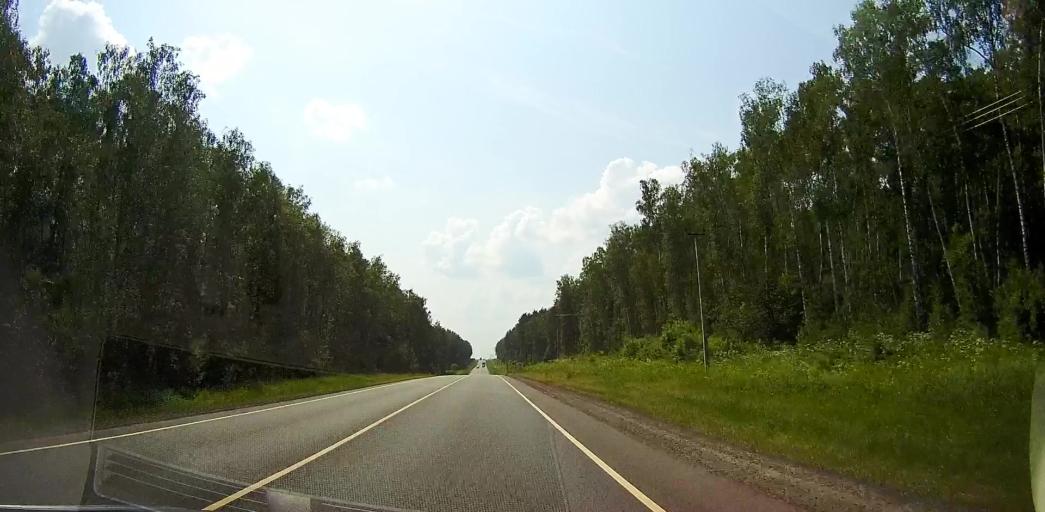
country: RU
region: Moskovskaya
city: Meshcherino
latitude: 55.1649
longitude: 38.3201
